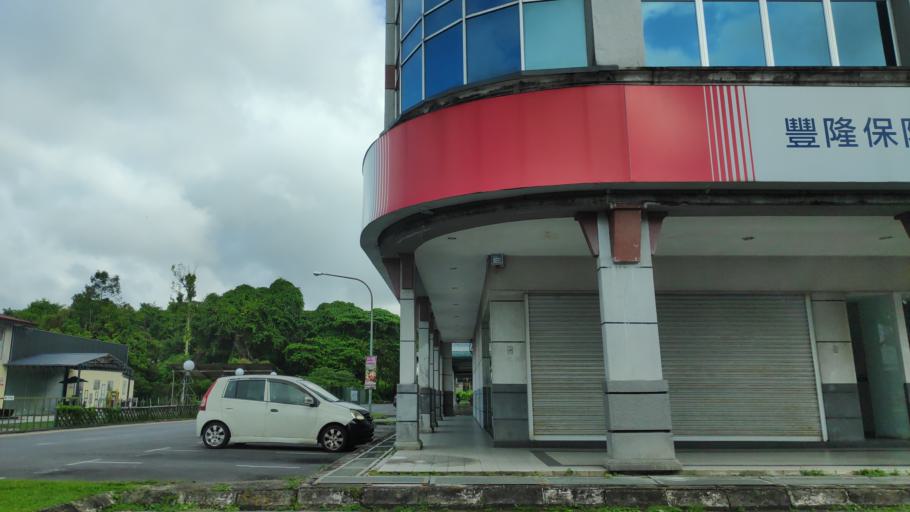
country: MY
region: Sarawak
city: Kuching
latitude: 1.5514
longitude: 110.3338
